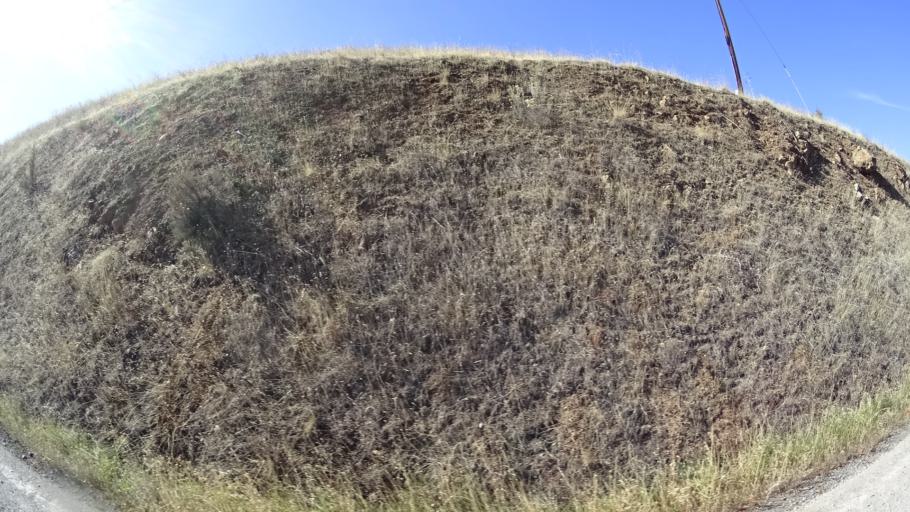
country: US
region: California
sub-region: Siskiyou County
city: Yreka
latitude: 41.7802
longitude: -122.5961
